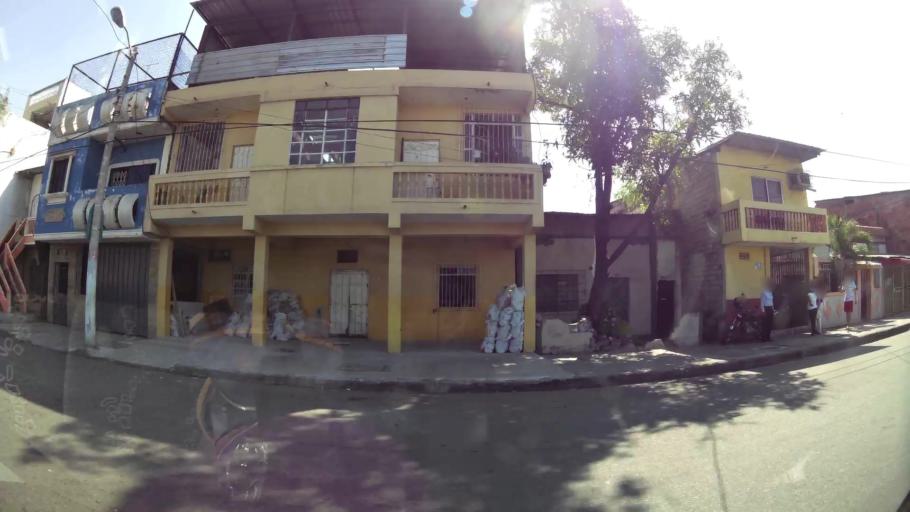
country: EC
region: Guayas
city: Guayaquil
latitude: -2.1924
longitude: -79.9109
